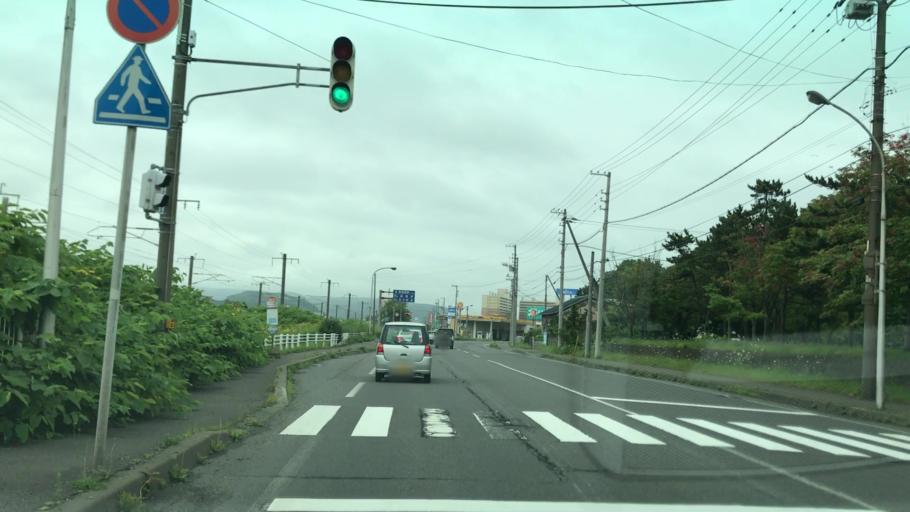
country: JP
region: Hokkaido
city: Muroran
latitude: 42.3396
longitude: 141.0158
